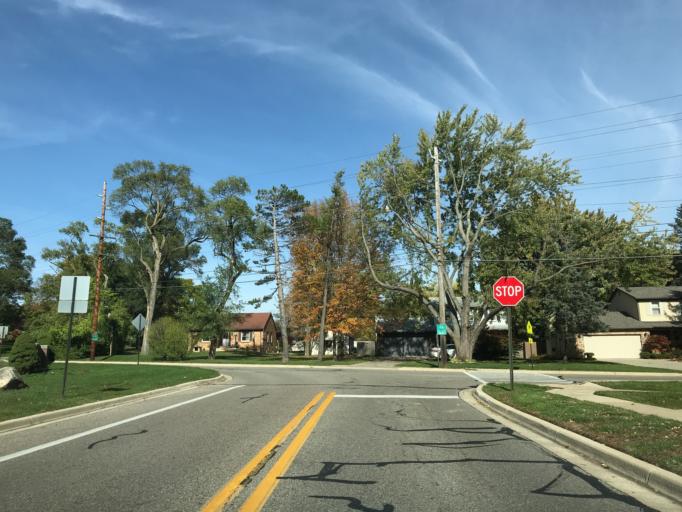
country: US
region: Michigan
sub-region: Oakland County
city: Farmington
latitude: 42.4649
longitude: -83.3667
